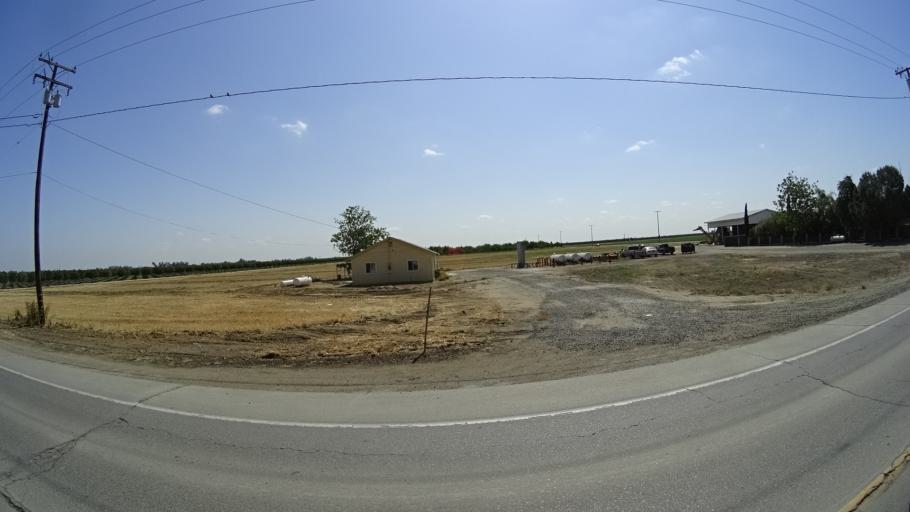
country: US
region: California
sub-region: Kings County
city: Home Garden
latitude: 36.2909
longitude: -119.6368
